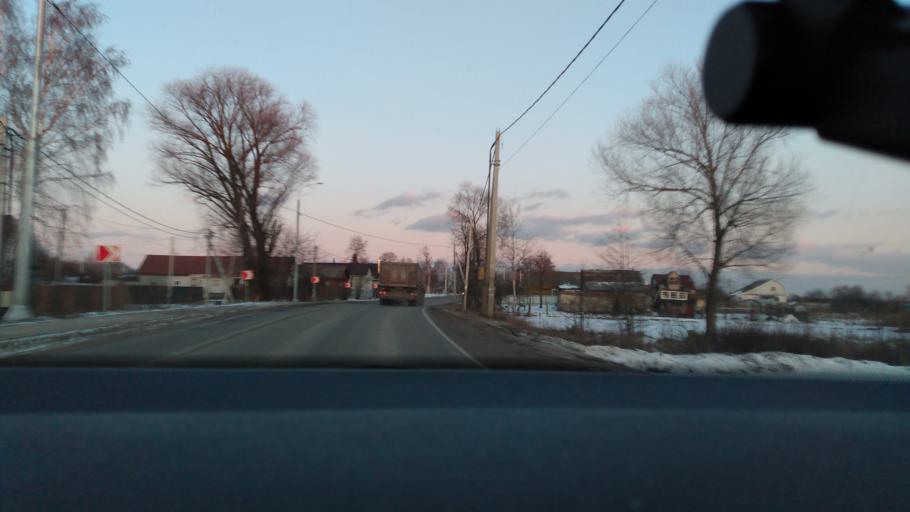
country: RU
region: Moskovskaya
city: Lukhovitsy
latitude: 55.1002
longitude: 38.9847
